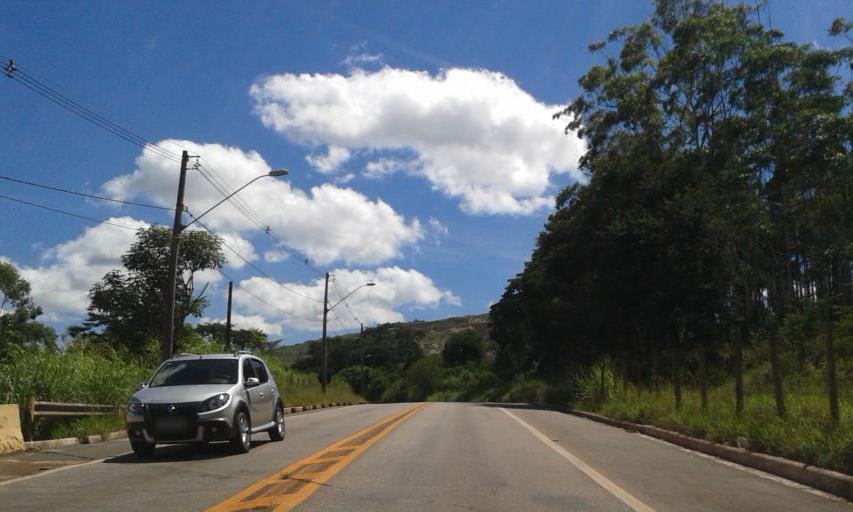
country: BR
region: Minas Gerais
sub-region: Itabira
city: Itabira
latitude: -19.6356
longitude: -43.2412
